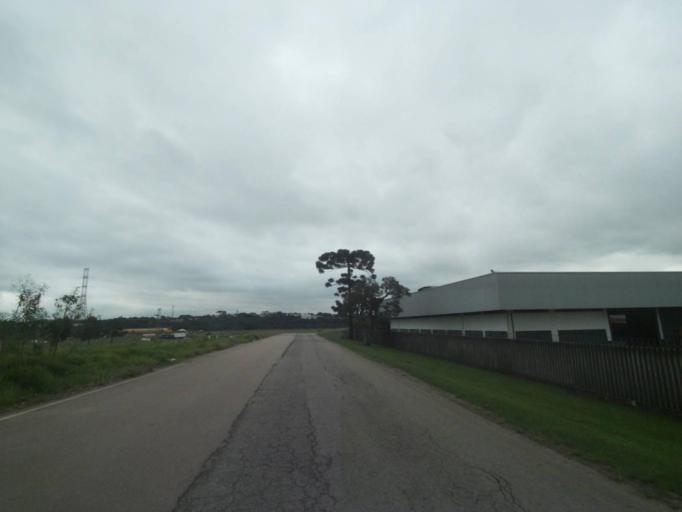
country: BR
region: Parana
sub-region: Araucaria
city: Araucaria
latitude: -25.5212
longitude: -49.3316
